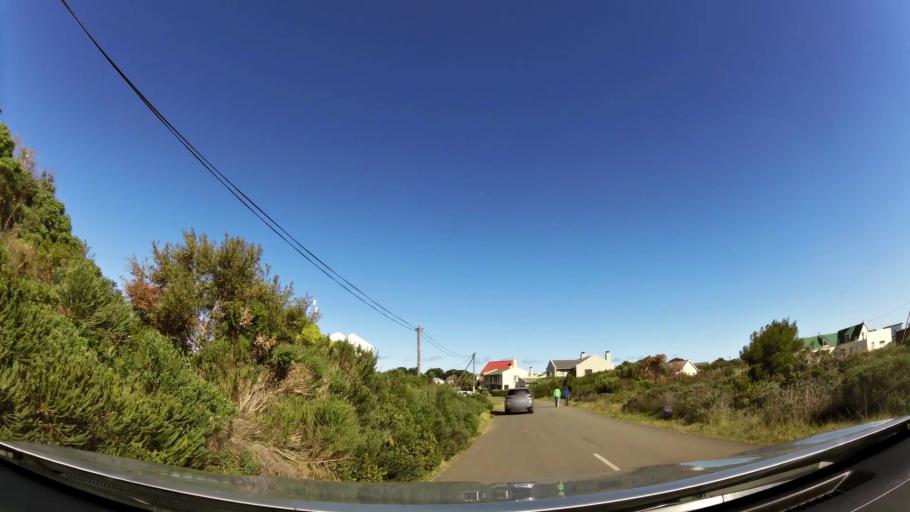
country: ZA
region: Western Cape
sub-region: Overberg District Municipality
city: Grabouw
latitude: -34.3704
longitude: 18.8922
